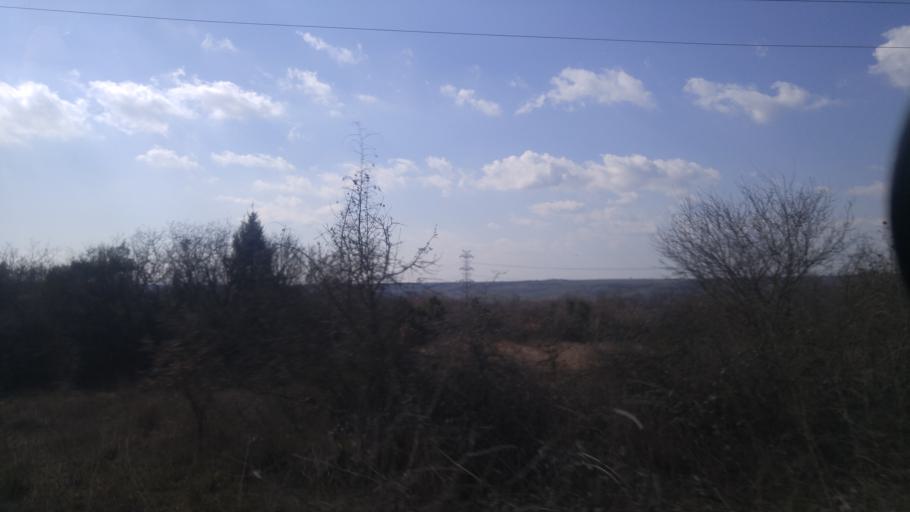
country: TR
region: Istanbul
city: Buyukcavuslu
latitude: 41.1844
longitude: 28.0860
